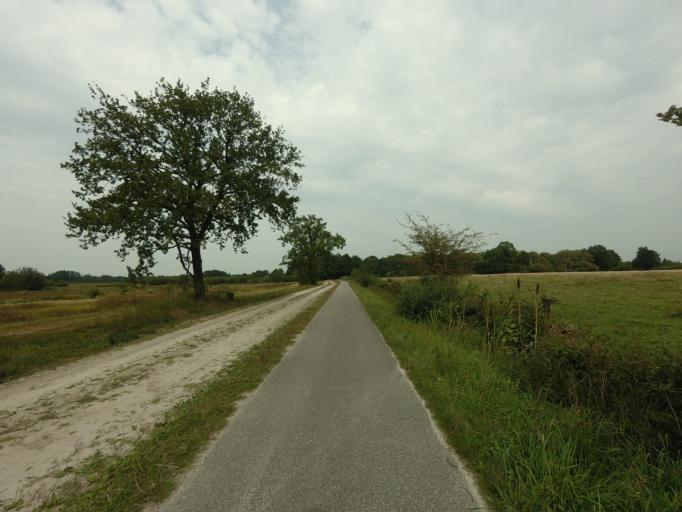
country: NL
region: Drenthe
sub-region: Gemeente Tynaarlo
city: Tynaarlo
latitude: 53.0185
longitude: 6.6329
